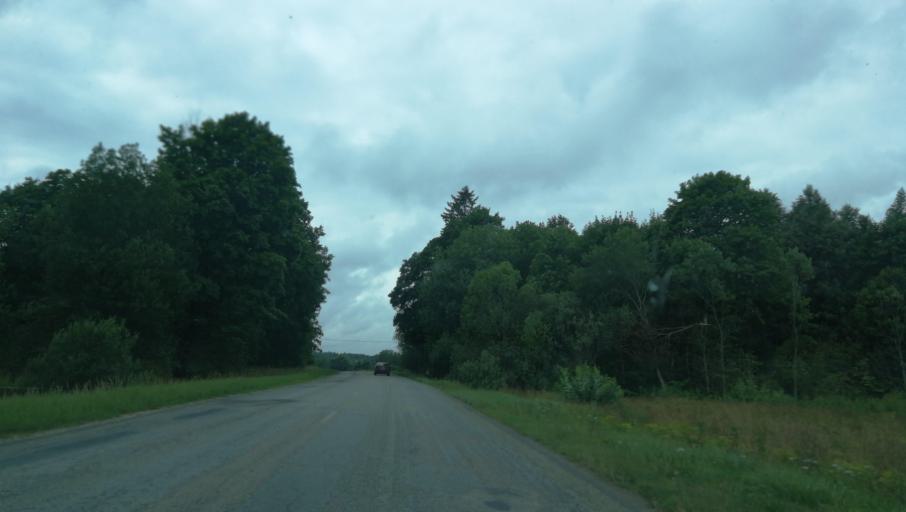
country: LV
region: Ogre
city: Jumprava
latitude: 56.7994
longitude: 25.0528
